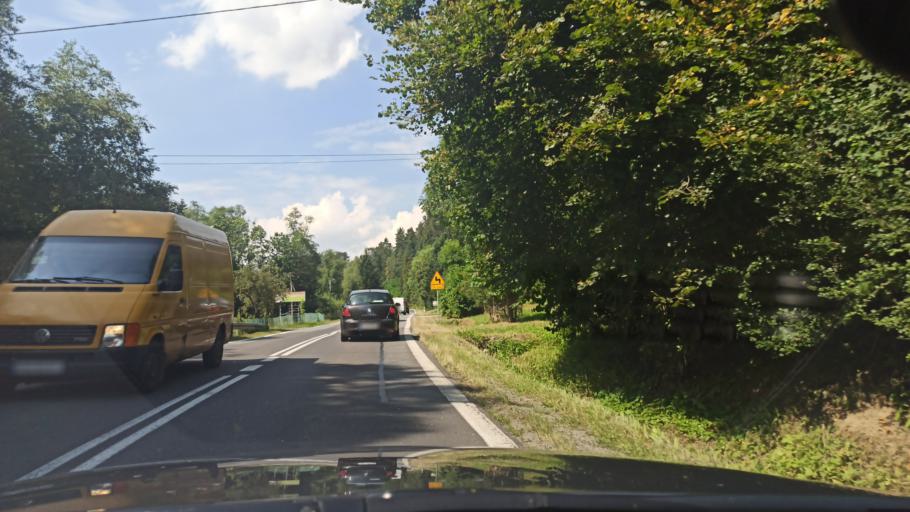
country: PL
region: Lesser Poland Voivodeship
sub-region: Powiat nowotarski
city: Krosnica
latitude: 49.4390
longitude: 20.3586
